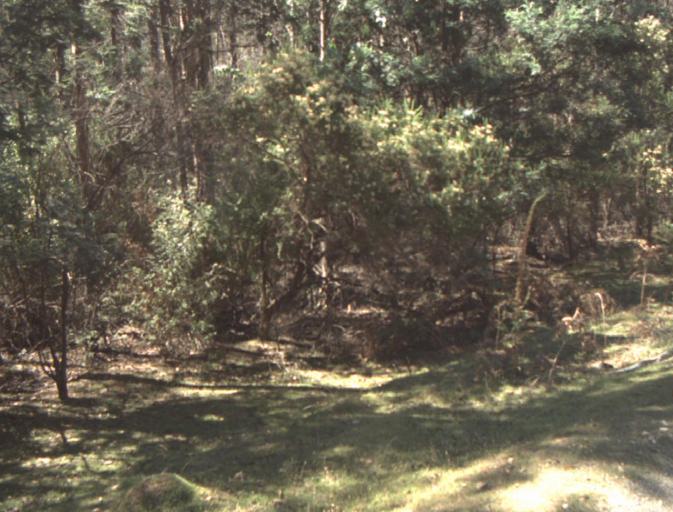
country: AU
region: Tasmania
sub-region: Dorset
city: Scottsdale
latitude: -41.2558
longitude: 147.3459
